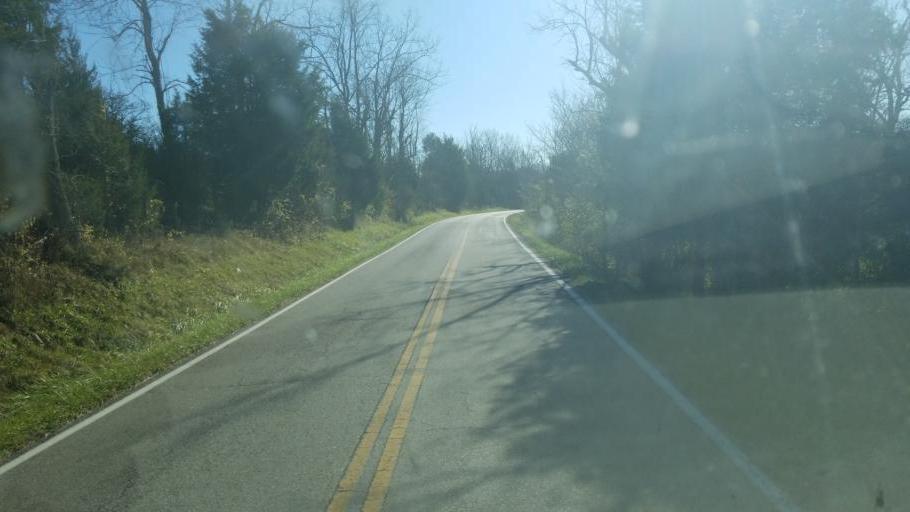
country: US
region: Ohio
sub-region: Adams County
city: Manchester
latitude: 38.5583
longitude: -83.6369
